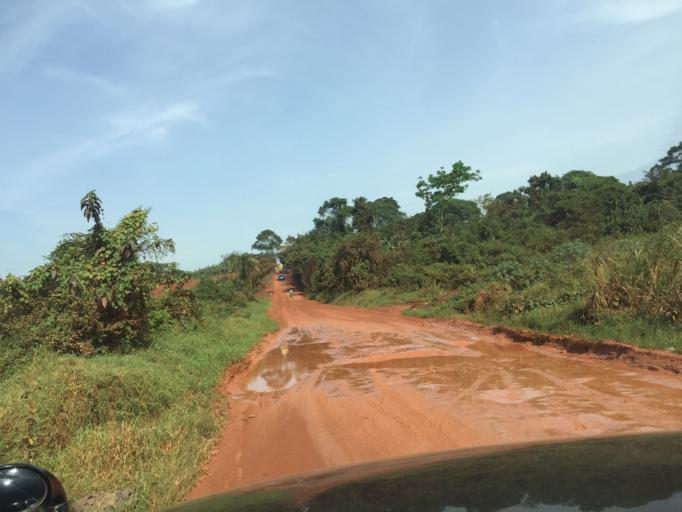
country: UG
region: Central Region
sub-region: Wakiso District
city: Wakiso
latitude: 0.4532
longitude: 32.5702
